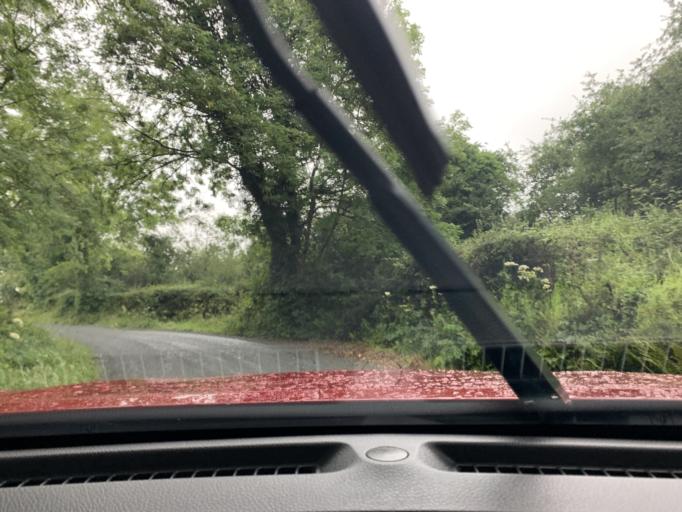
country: IE
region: Connaught
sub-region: Sligo
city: Sligo
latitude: 54.3066
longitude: -8.4586
